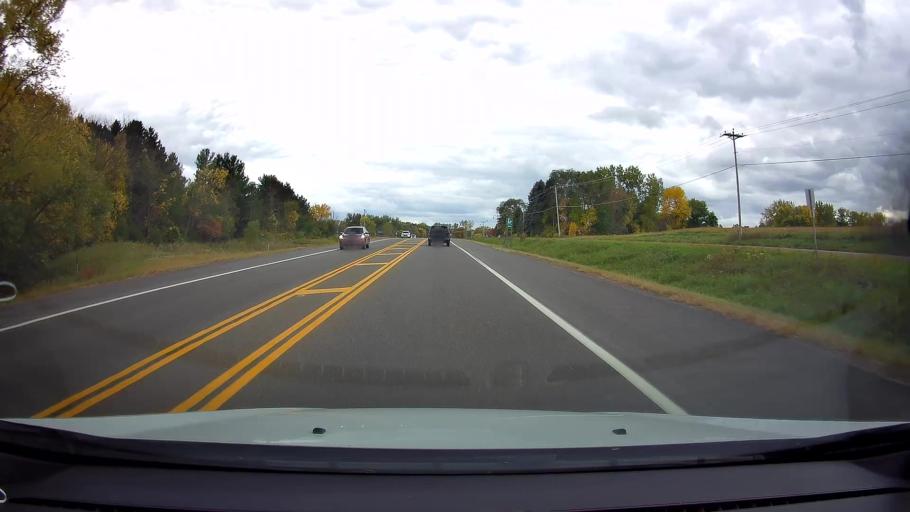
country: US
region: Minnesota
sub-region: Chisago County
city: Lindstrom
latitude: 45.3862
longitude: -92.8678
